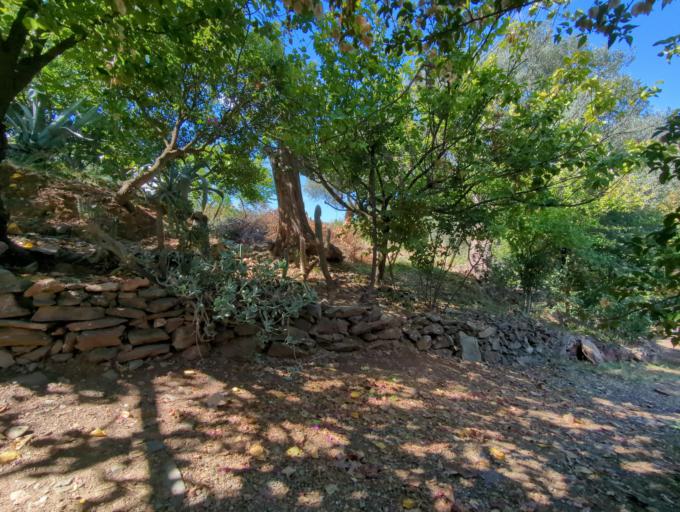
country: GR
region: Crete
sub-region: Nomos Chanias
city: Galatas
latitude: 35.4194
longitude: 23.9391
